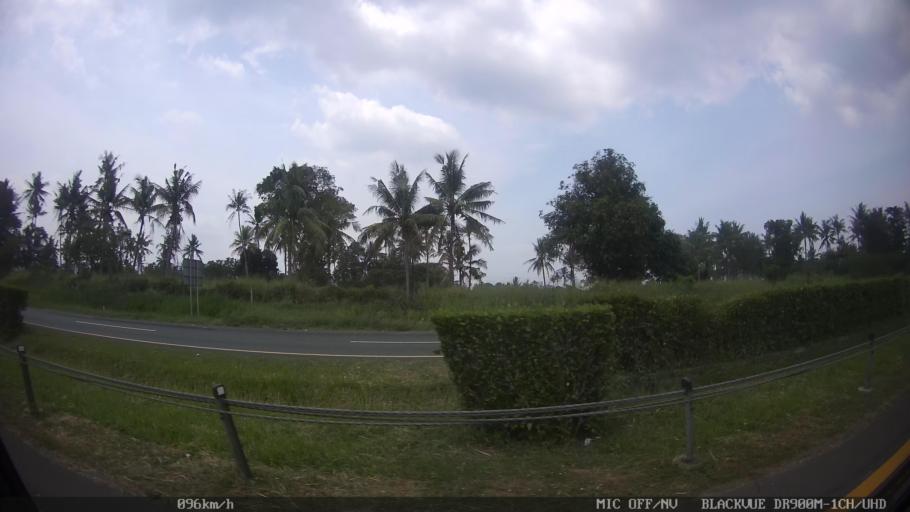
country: ID
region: Banten
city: Curug
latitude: -5.9957
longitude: 106.0558
